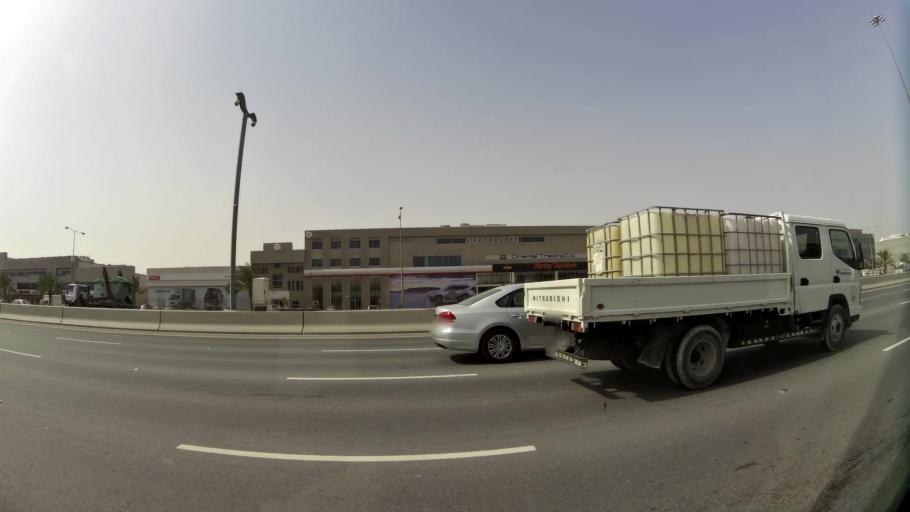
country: QA
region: Baladiyat ad Dawhah
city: Doha
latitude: 25.2523
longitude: 51.4776
